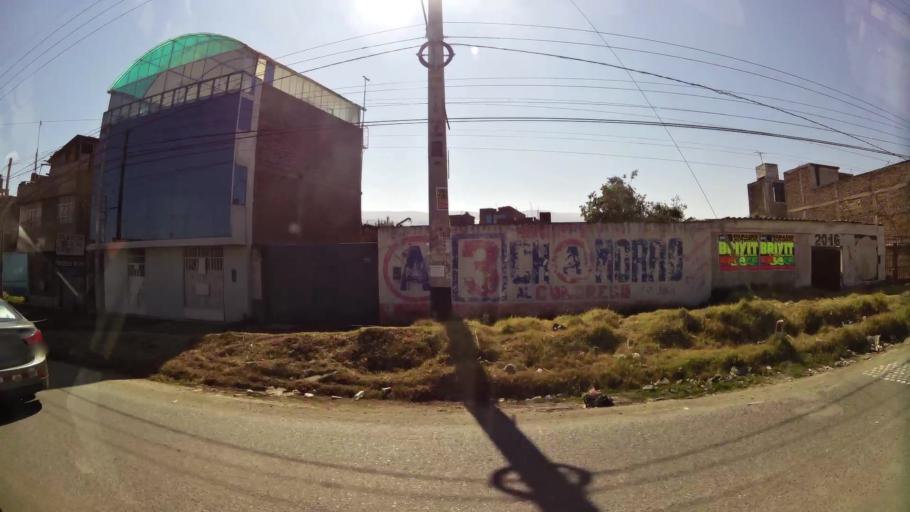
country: PE
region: Junin
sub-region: Provincia de Huancayo
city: San Agustin
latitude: -12.0038
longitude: -75.2504
